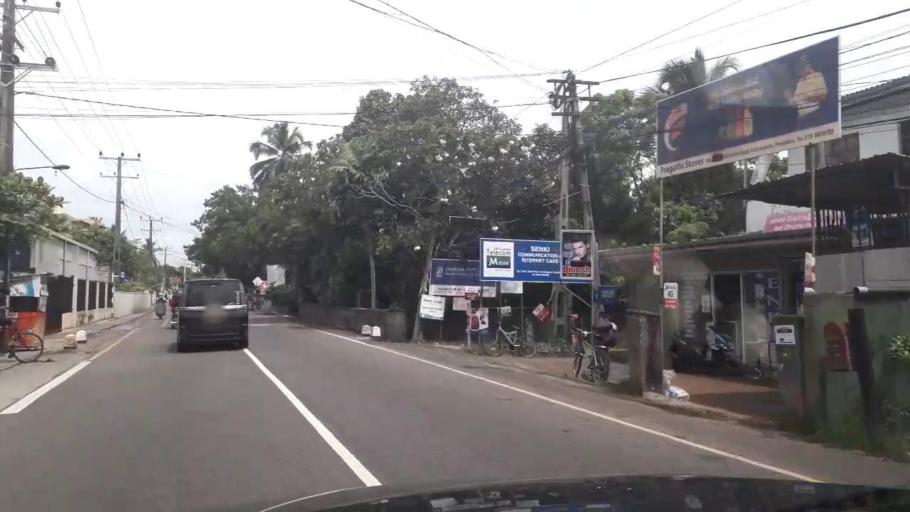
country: LK
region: Western
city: Panadura
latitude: 6.7364
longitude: 79.9040
